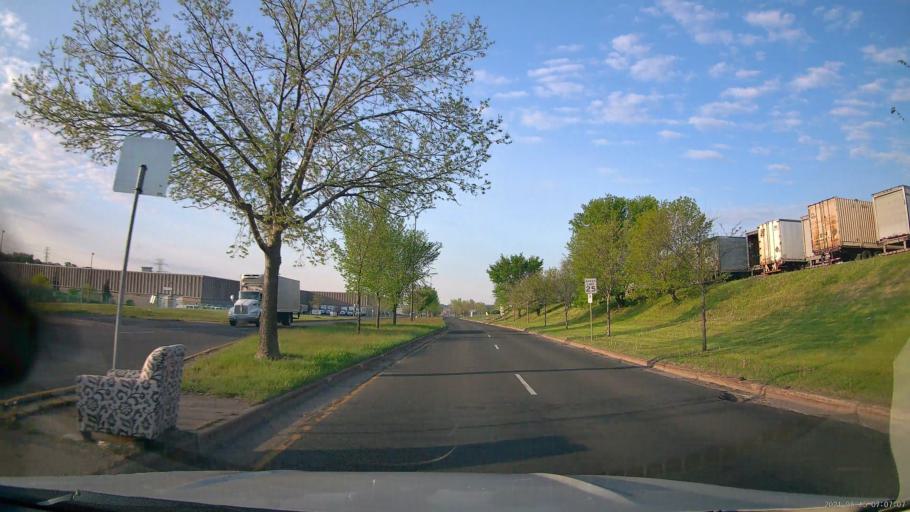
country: US
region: Minnesota
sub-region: Ramsey County
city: Lauderdale
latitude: 44.9999
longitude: -93.2116
